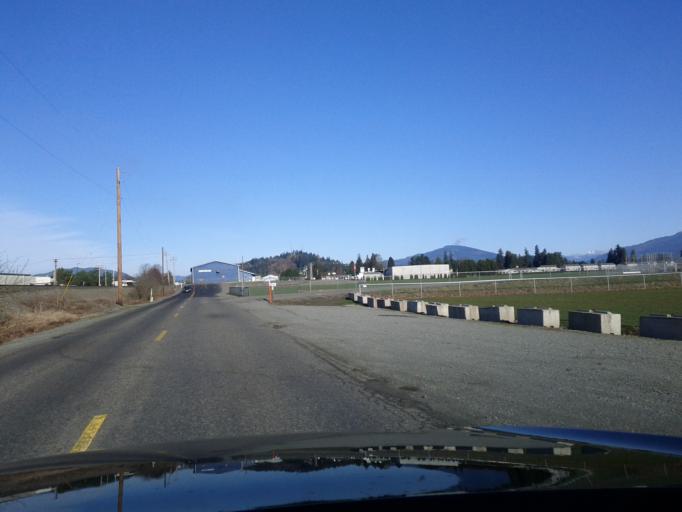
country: US
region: Washington
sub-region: Skagit County
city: Burlington
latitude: 48.4549
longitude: -122.3250
